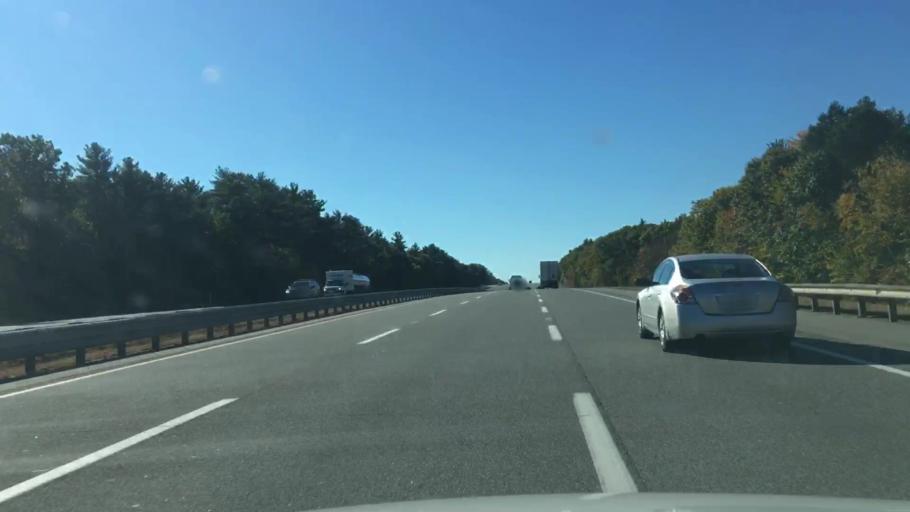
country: US
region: Maine
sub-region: York County
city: Cape Neddick
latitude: 43.2207
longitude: -70.6381
